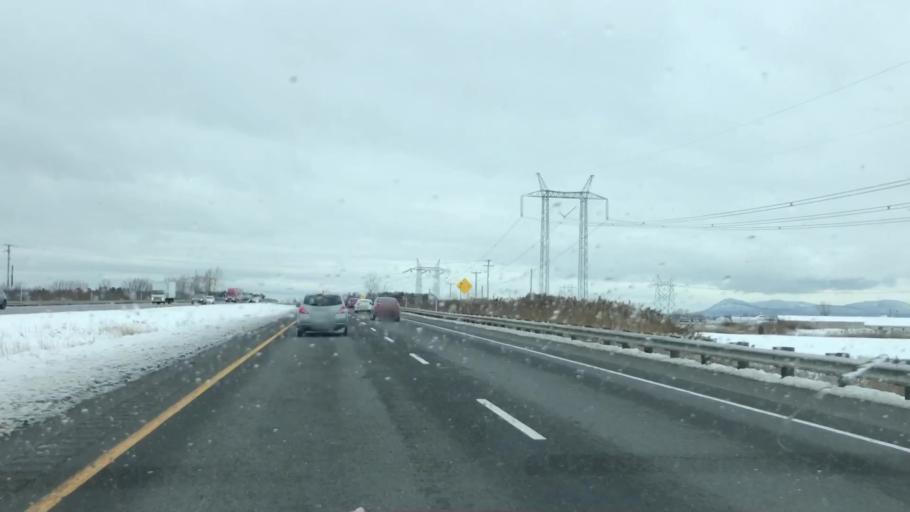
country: CA
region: Quebec
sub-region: Monteregie
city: Rougemont
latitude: 45.4120
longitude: -73.1062
